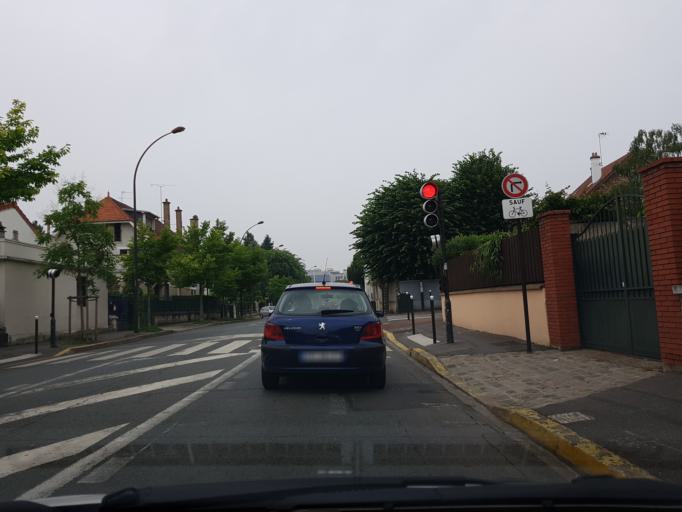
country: FR
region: Ile-de-France
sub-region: Departement des Hauts-de-Seine
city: Bourg-la-Reine
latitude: 48.7806
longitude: 2.3216
